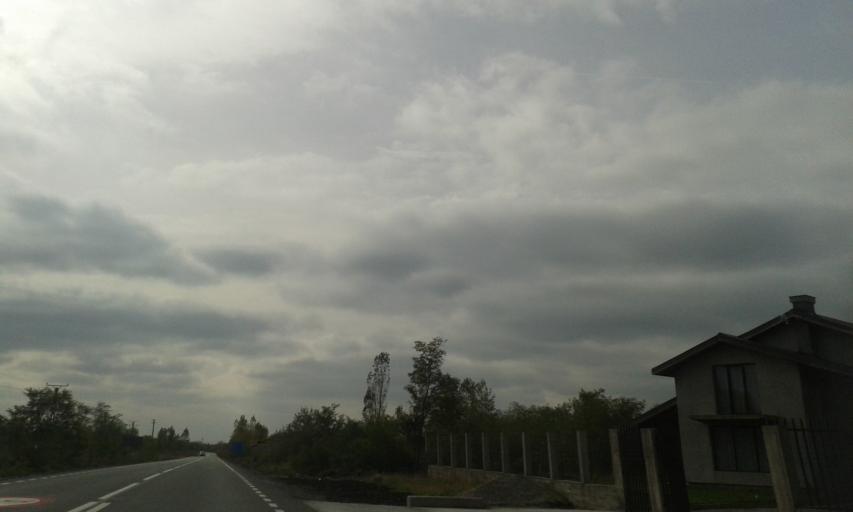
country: RO
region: Gorj
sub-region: Comuna Bumbesti-Jiu
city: Bumbesti-Jiu
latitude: 45.1665
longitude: 23.3806
